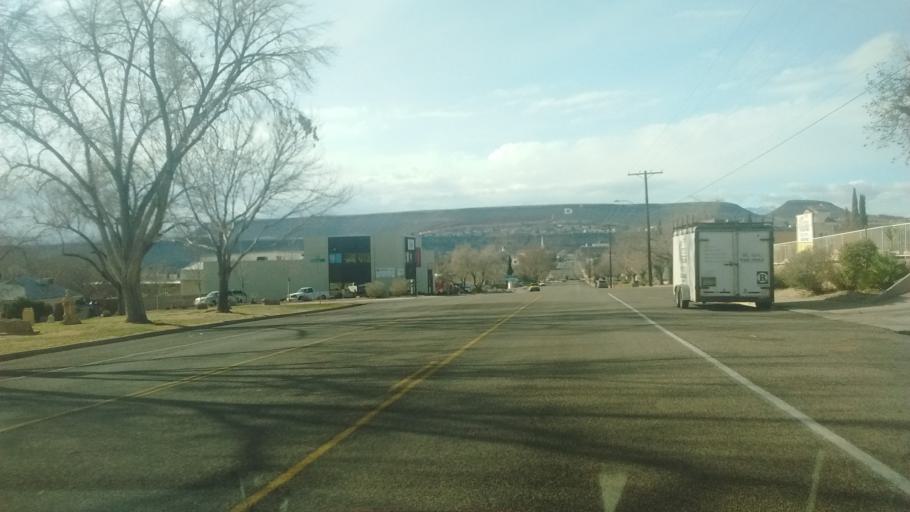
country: US
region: Utah
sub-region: Washington County
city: Saint George
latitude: 37.1082
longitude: -113.5698
